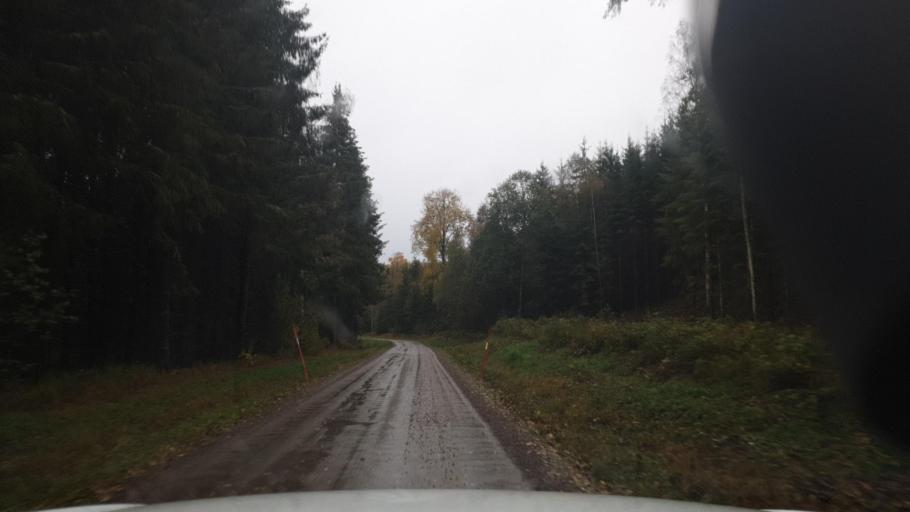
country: SE
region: Vaermland
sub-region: Eda Kommun
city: Amotfors
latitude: 59.7853
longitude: 12.4281
